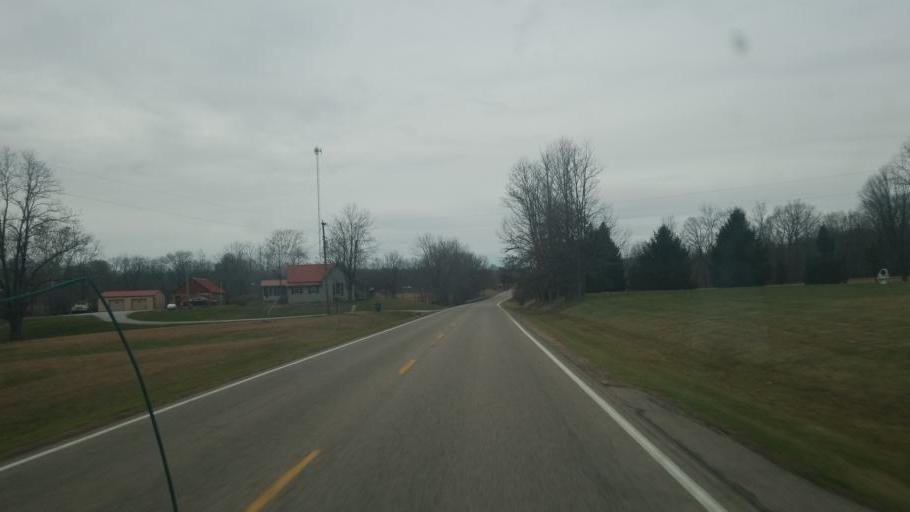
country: US
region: Indiana
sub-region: Clay County
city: Middlebury
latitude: 39.3607
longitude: -86.9522
